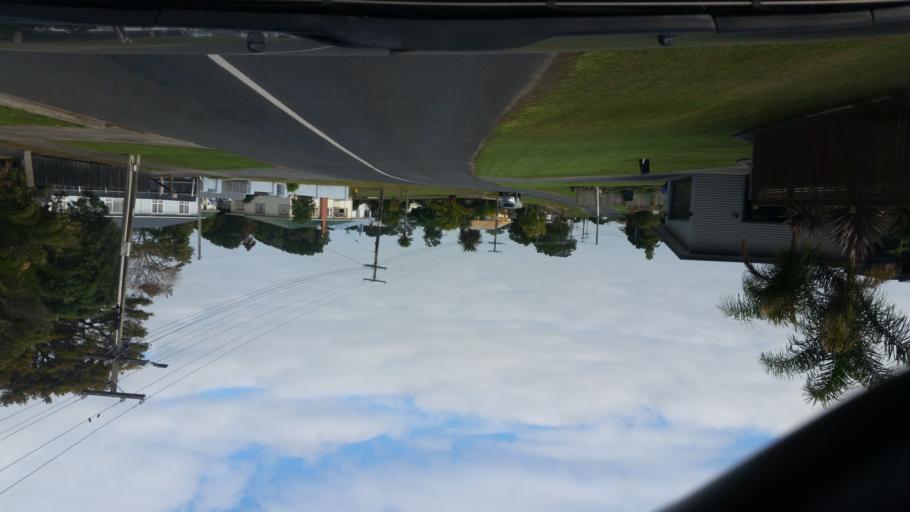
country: NZ
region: Northland
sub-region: Kaipara District
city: Dargaville
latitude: -35.9277
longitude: 173.8692
